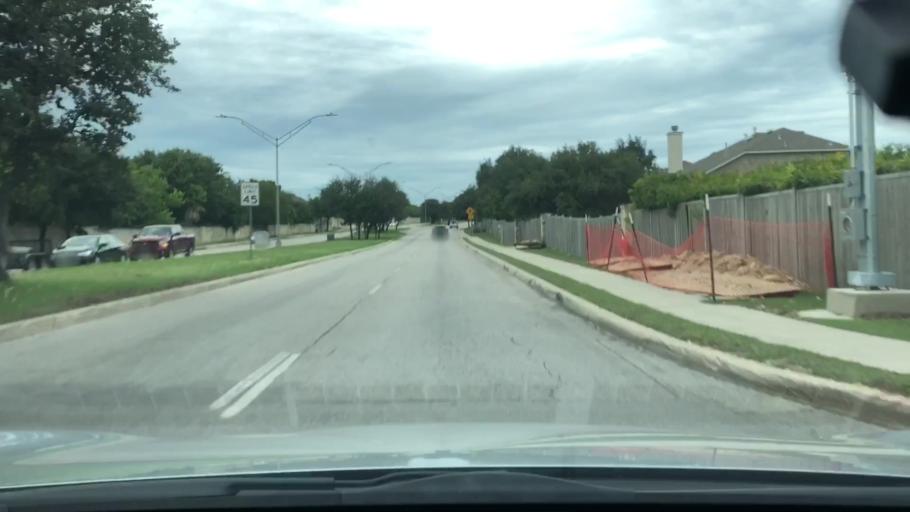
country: US
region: Texas
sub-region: Bexar County
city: Leon Valley
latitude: 29.4599
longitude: -98.6718
